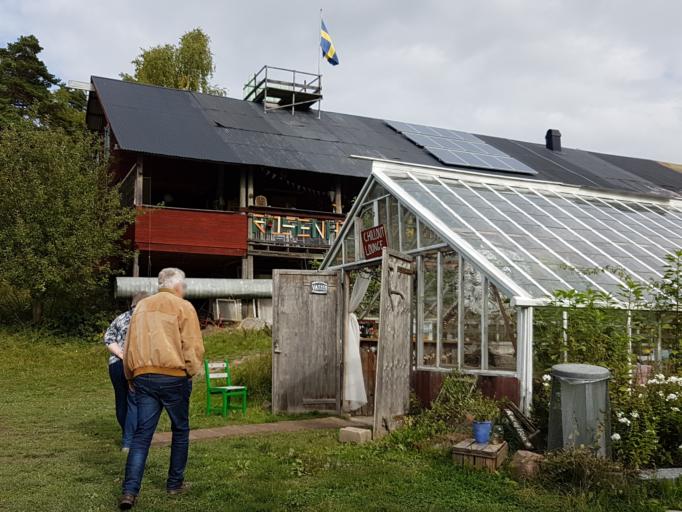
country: SE
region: Stockholm
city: Stenhamra
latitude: 59.2948
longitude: 17.7160
